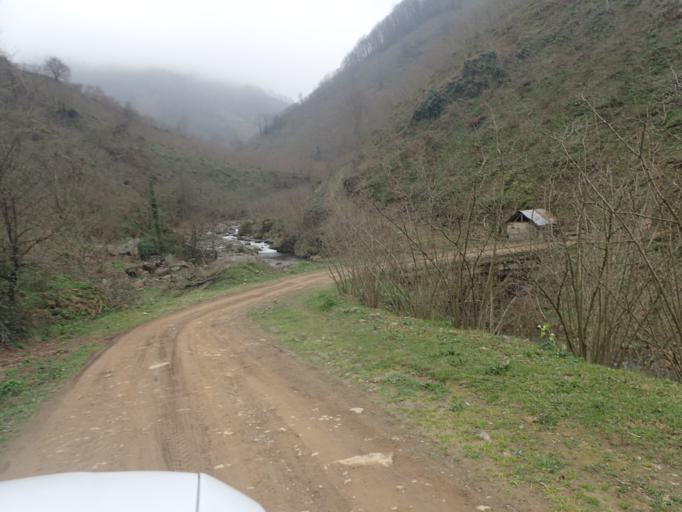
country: TR
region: Ordu
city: Camas
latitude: 40.9000
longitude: 37.5540
